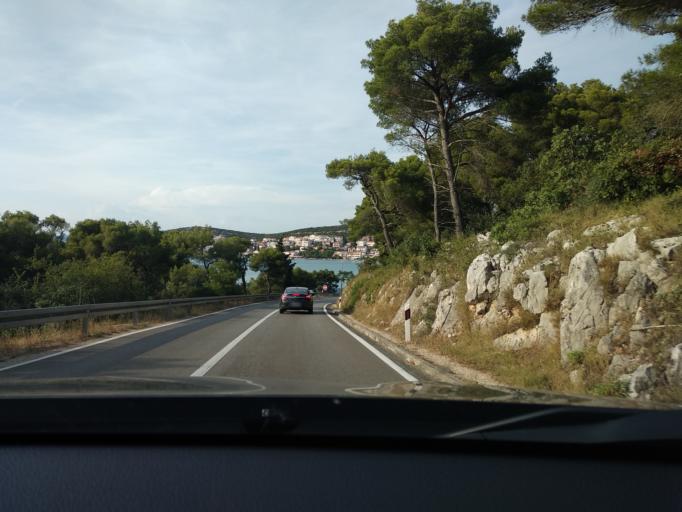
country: HR
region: Sibensko-Kniniska
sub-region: Grad Sibenik
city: Tisno
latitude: 43.7958
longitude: 15.6335
